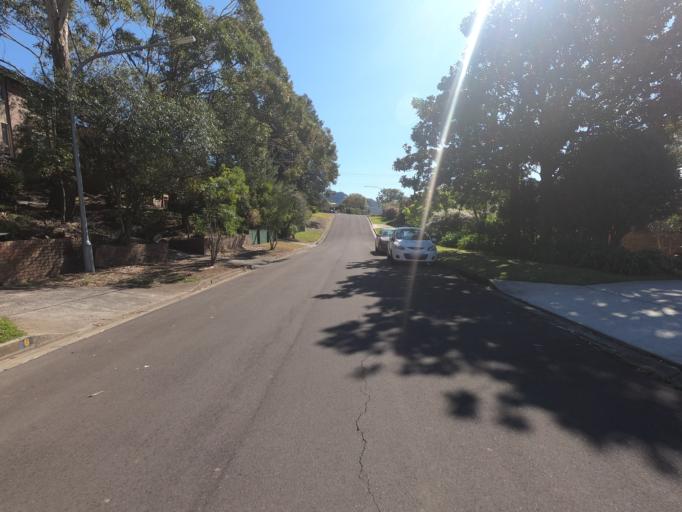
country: AU
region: New South Wales
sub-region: Wollongong
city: Mount Ousley
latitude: -34.3984
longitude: 150.8713
